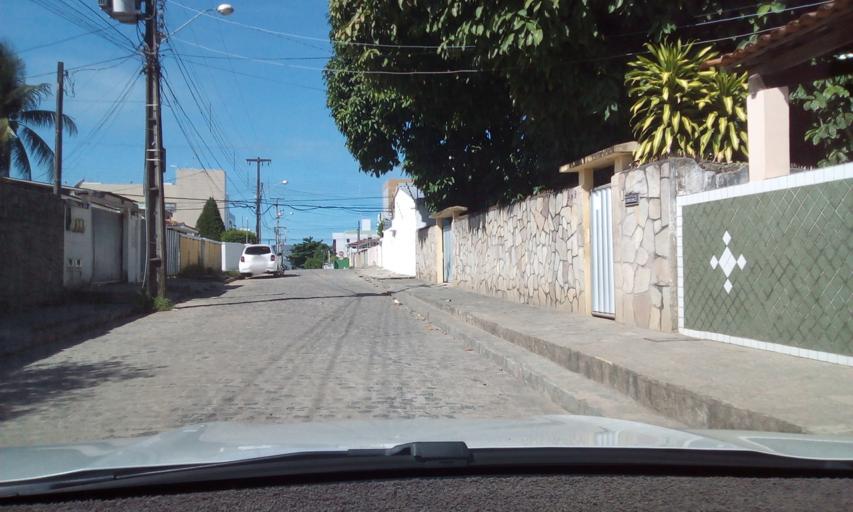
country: BR
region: Paraiba
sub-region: Joao Pessoa
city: Joao Pessoa
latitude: -7.1533
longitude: -34.8474
